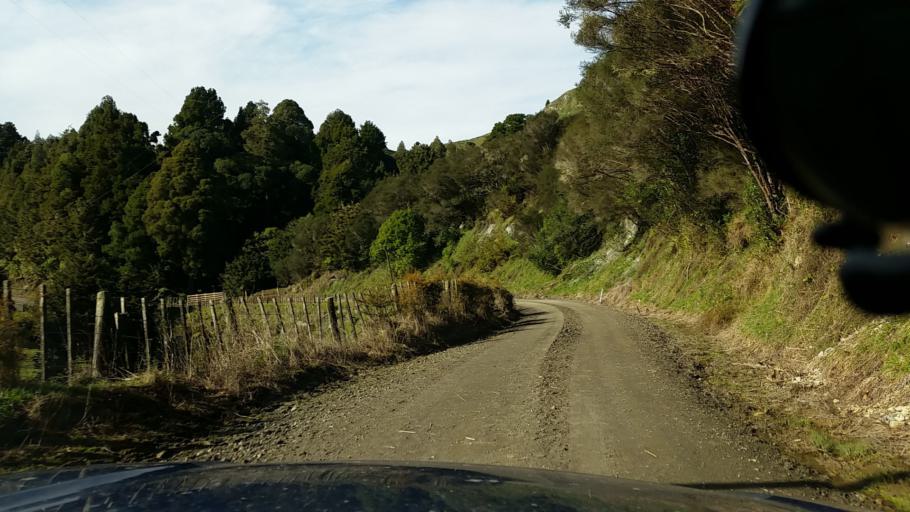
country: NZ
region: Taranaki
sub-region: New Plymouth District
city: Waitara
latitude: -39.0510
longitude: 174.7597
